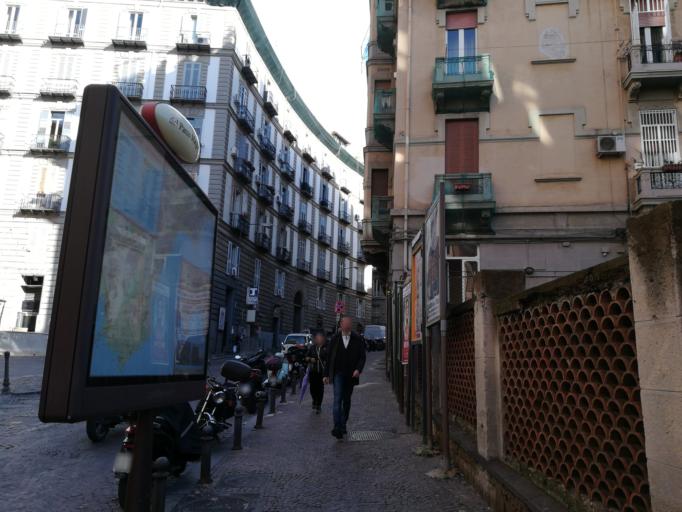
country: IT
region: Campania
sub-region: Provincia di Napoli
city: Napoli
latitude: 40.8377
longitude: 14.2345
